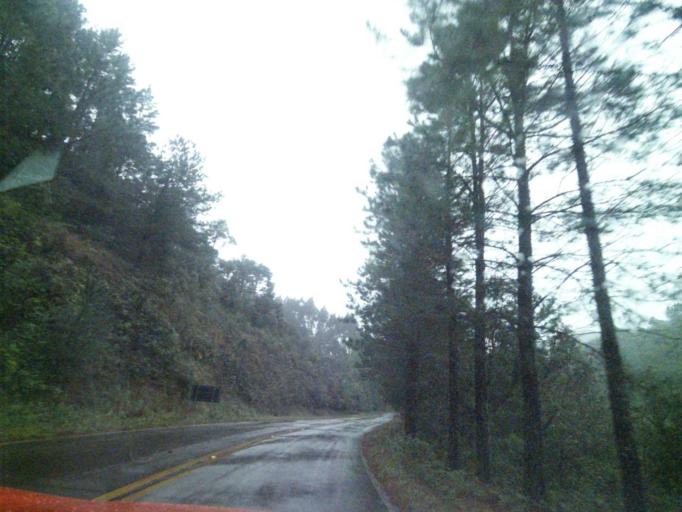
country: BR
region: Santa Catarina
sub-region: Anitapolis
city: Anitapolis
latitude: -27.7955
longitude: -49.0444
